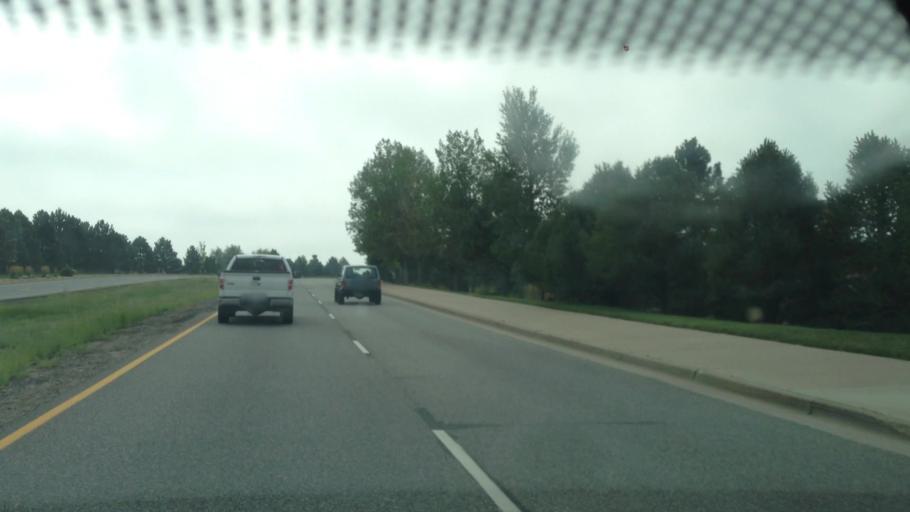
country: US
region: Colorado
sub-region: Douglas County
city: Parker
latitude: 39.6051
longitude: -104.7293
